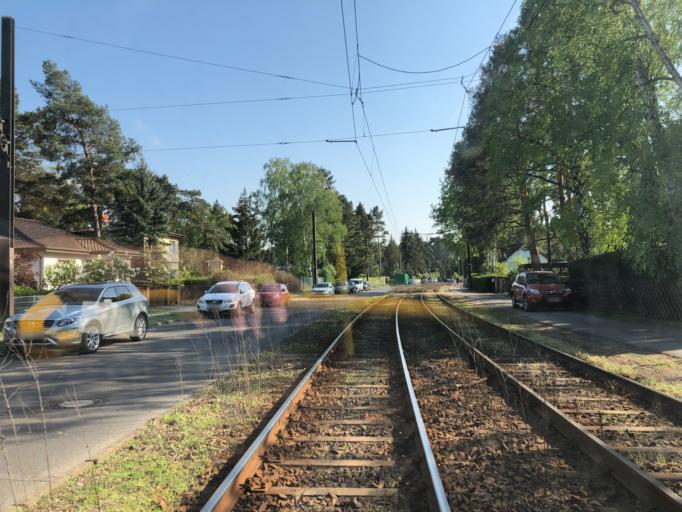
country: DE
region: Berlin
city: Schmockwitz
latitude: 52.3892
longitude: 13.6352
